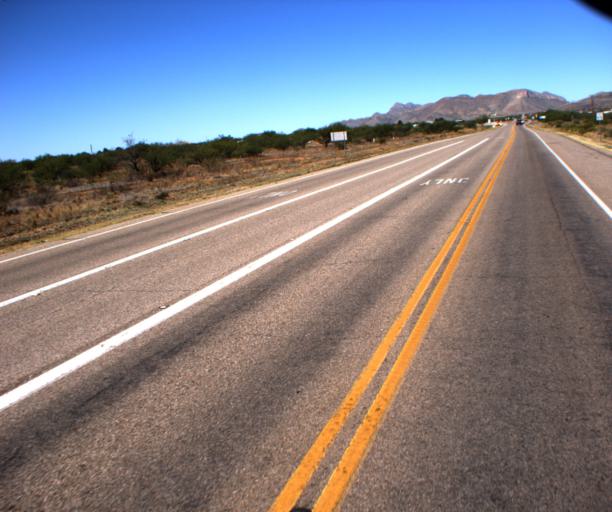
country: US
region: Arizona
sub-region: Cochise County
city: Huachuca City
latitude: 31.6928
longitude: -110.3510
